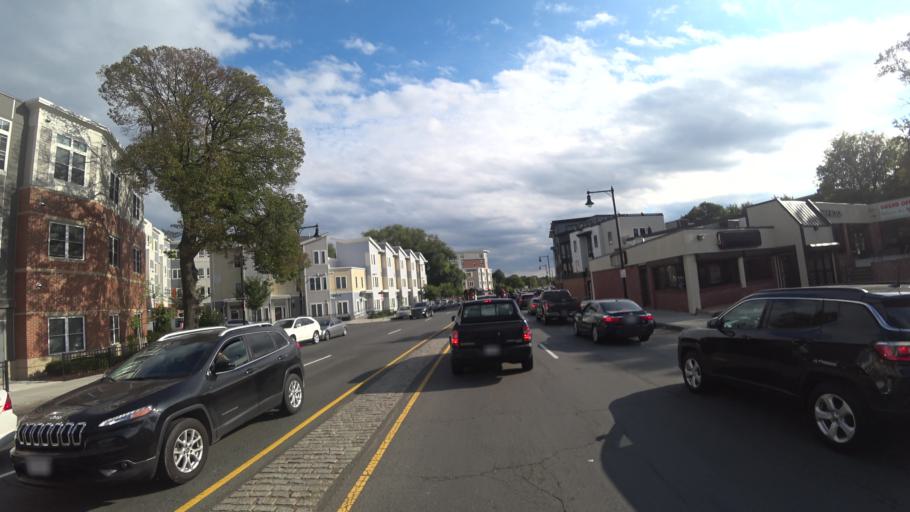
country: US
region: Massachusetts
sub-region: Suffolk County
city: South Boston
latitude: 42.3313
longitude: -71.0530
